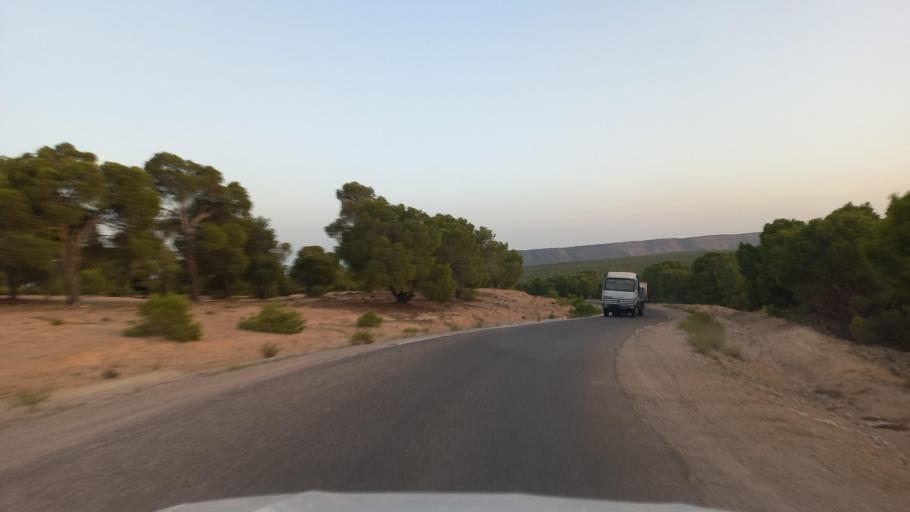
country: TN
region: Al Qasrayn
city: Sbiba
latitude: 35.4214
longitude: 8.9241
